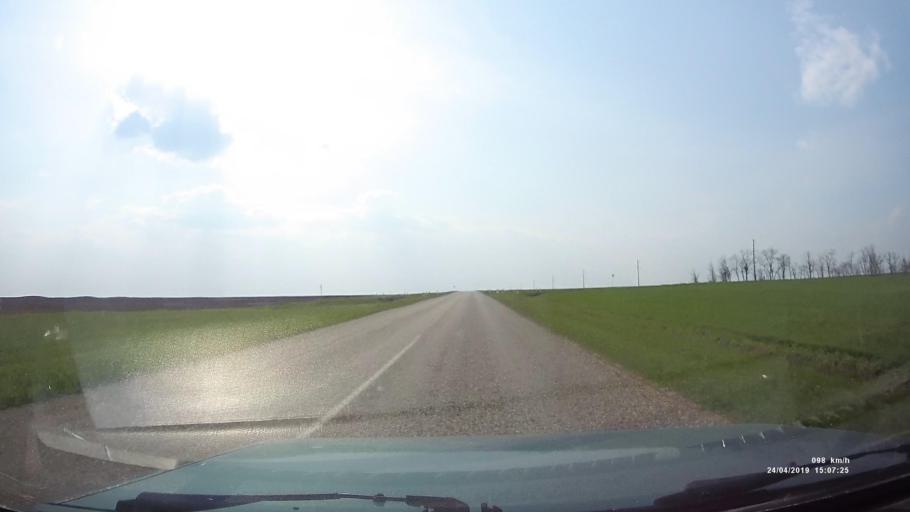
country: RU
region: Rostov
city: Remontnoye
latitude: 46.5594
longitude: 43.4058
